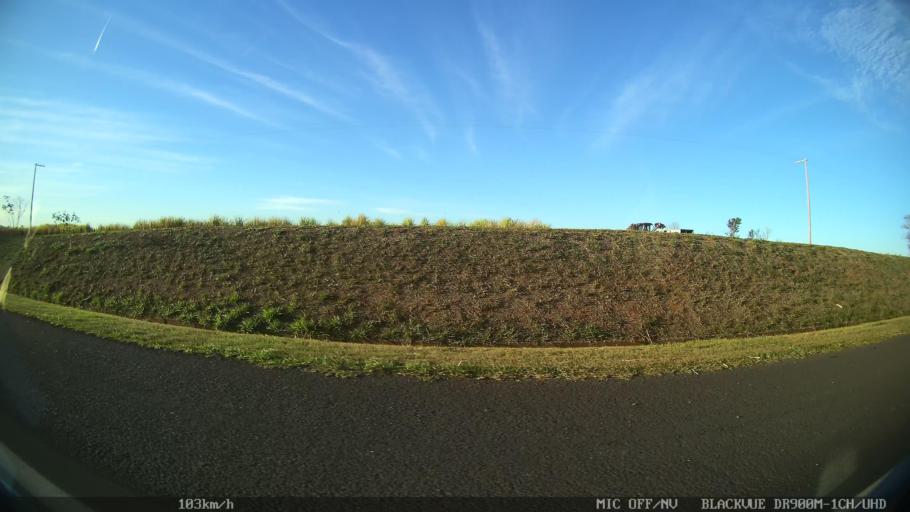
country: BR
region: Sao Paulo
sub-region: Catanduva
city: Catanduva
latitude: -21.0373
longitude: -49.1452
